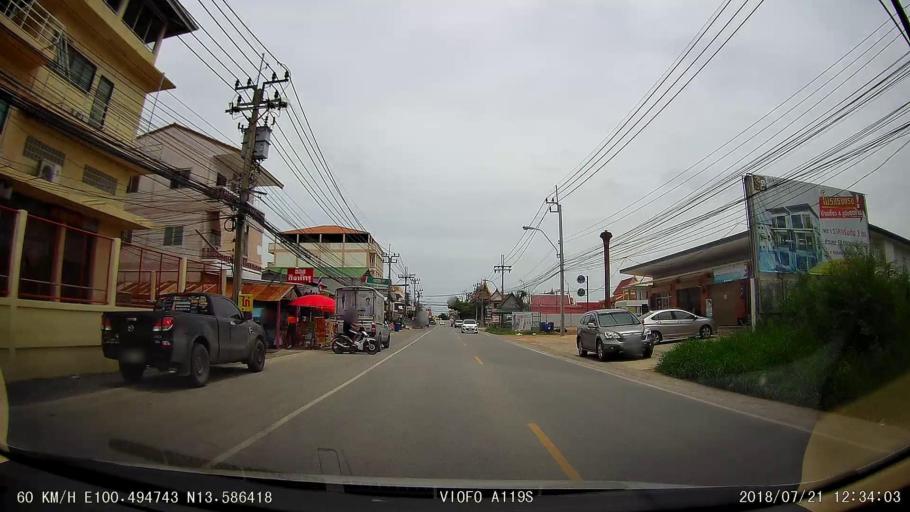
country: TH
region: Bangkok
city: Thung Khru
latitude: 13.5864
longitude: 100.4946
